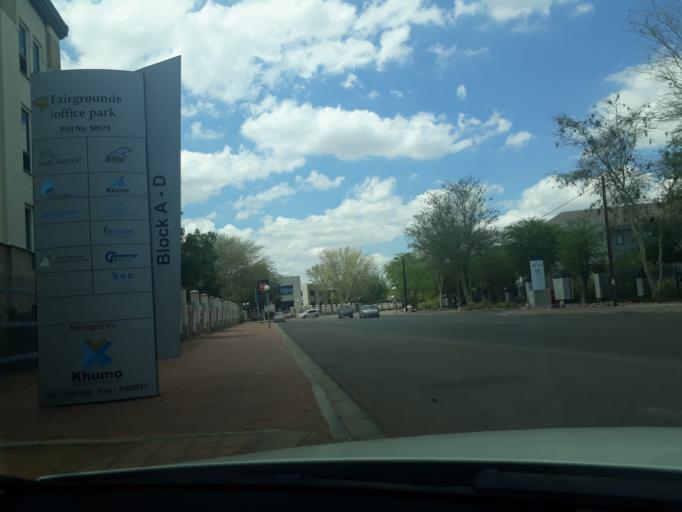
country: BW
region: South East
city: Gaborone
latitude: -24.6784
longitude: 25.9257
